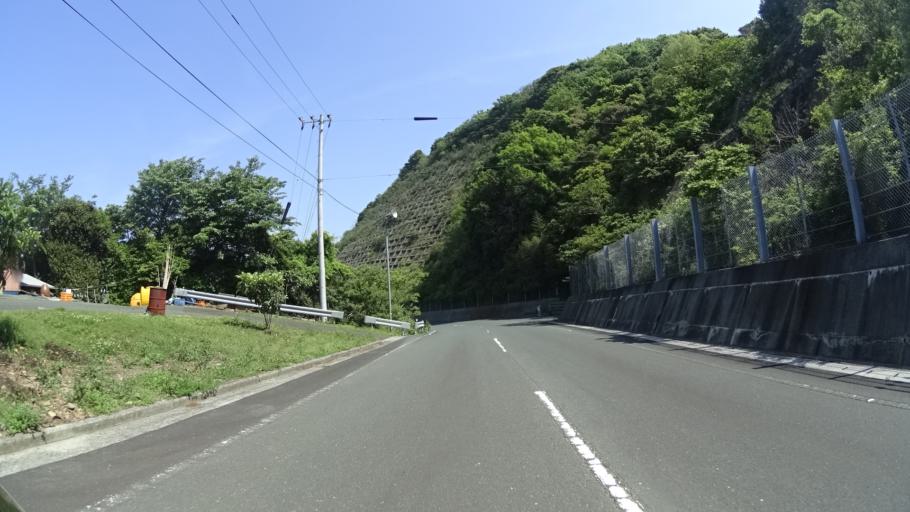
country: JP
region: Oita
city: Tsukumiura
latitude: 33.3605
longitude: 132.0395
